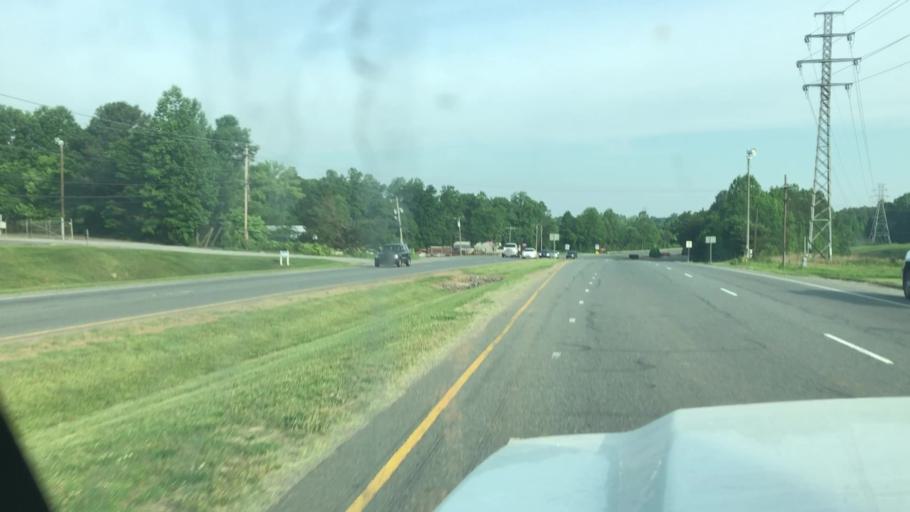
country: US
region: North Carolina
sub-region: Mecklenburg County
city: Charlotte
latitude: 35.2934
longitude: -80.9163
